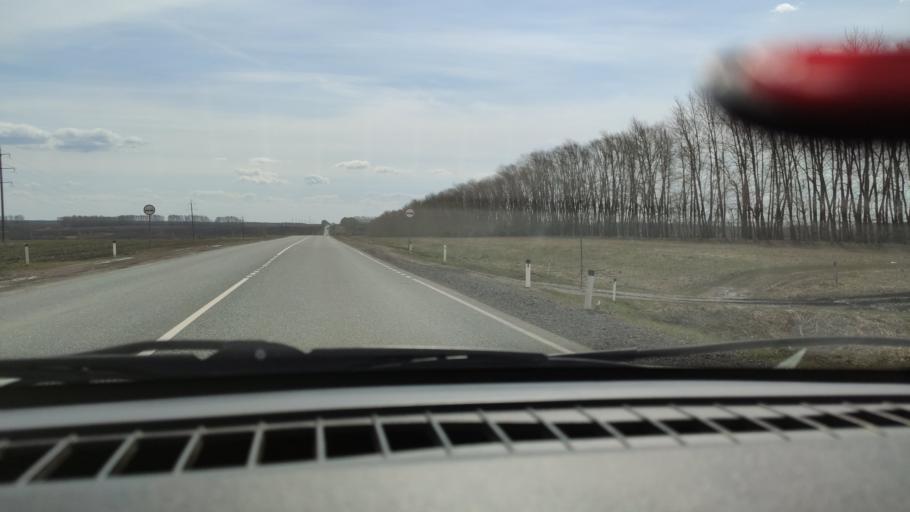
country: RU
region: Bashkortostan
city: Dyurtyuli
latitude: 55.2606
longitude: 55.0608
